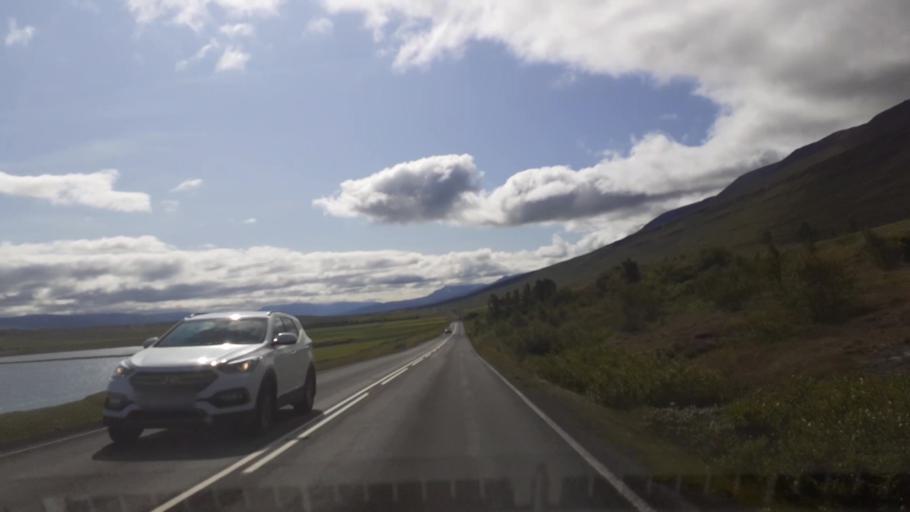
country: IS
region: Northeast
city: Akureyri
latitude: 65.8744
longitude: -18.2644
